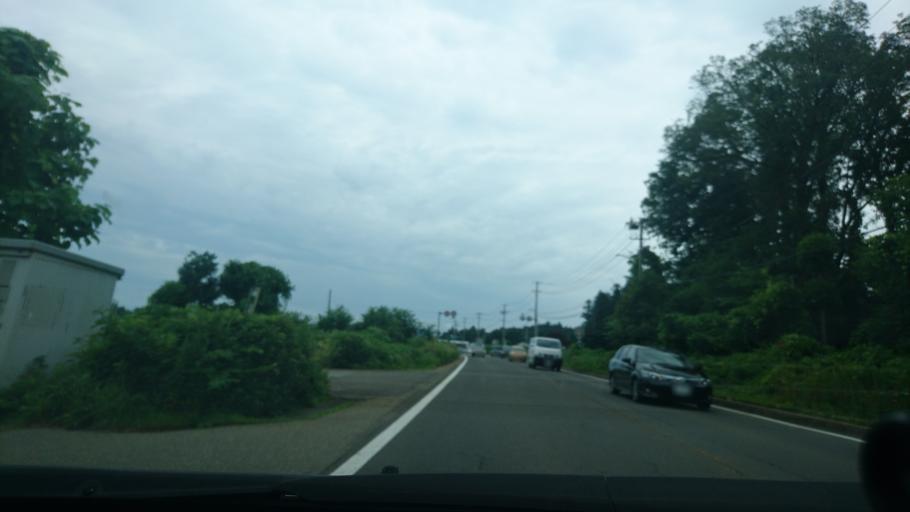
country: JP
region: Akita
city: Yokotemachi
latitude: 39.3447
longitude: 140.5607
